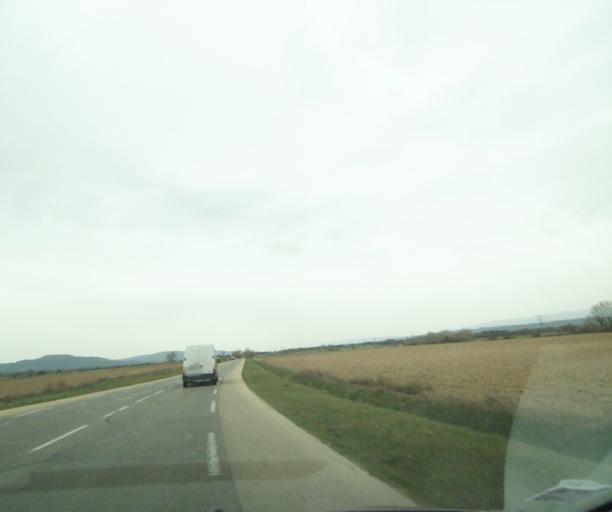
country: FR
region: Provence-Alpes-Cote d'Azur
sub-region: Departement des Bouches-du-Rhone
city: Meyrargues
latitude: 43.6511
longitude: 5.5218
